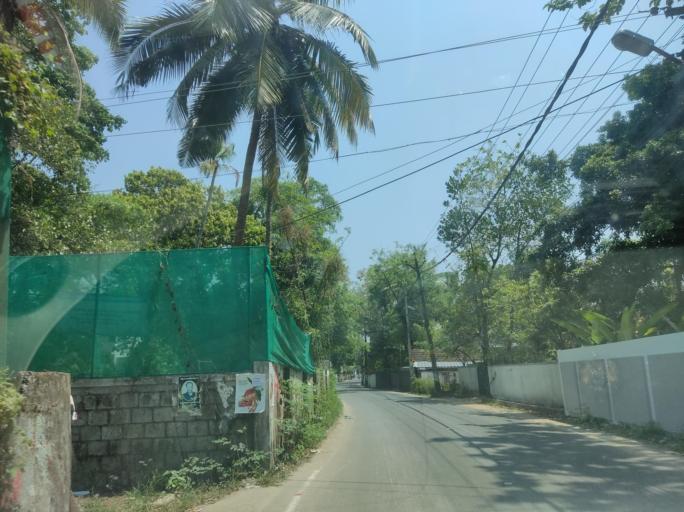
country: IN
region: Kerala
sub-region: Alappuzha
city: Arukutti
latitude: 9.8572
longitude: 76.2930
